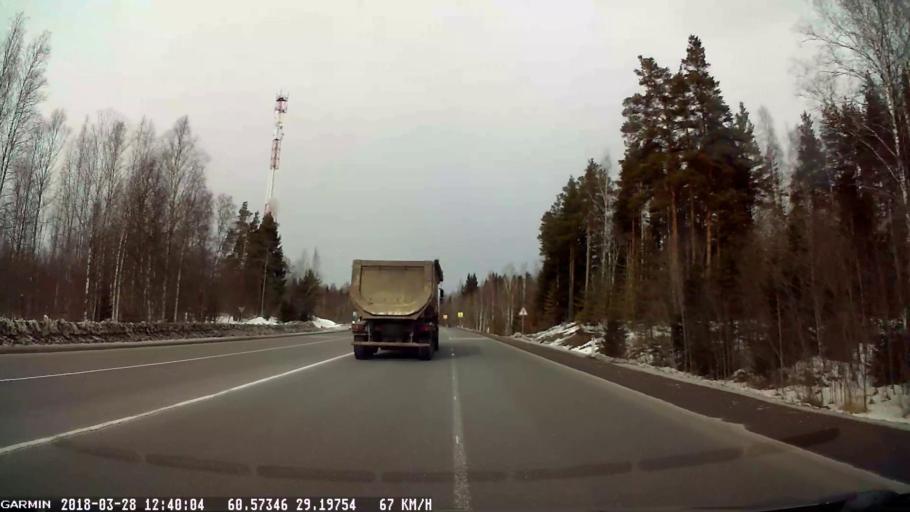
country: RU
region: Leningrad
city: Veshchevo
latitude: 60.5735
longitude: 29.1974
